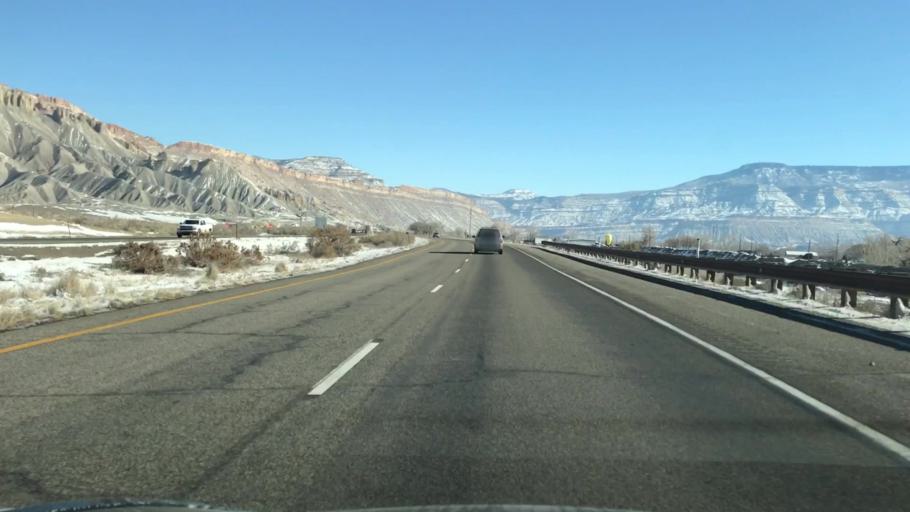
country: US
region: Colorado
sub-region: Mesa County
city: Clifton
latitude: 39.1077
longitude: -108.4300
